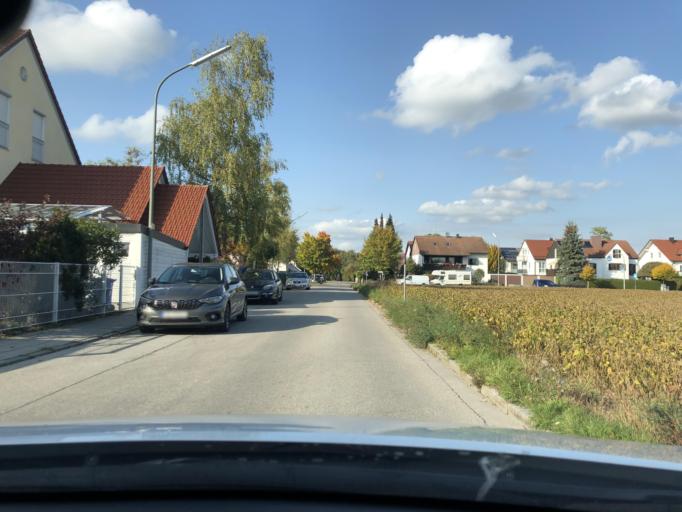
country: DE
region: Bavaria
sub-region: Upper Bavaria
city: Maisach
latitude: 48.2193
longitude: 11.2604
